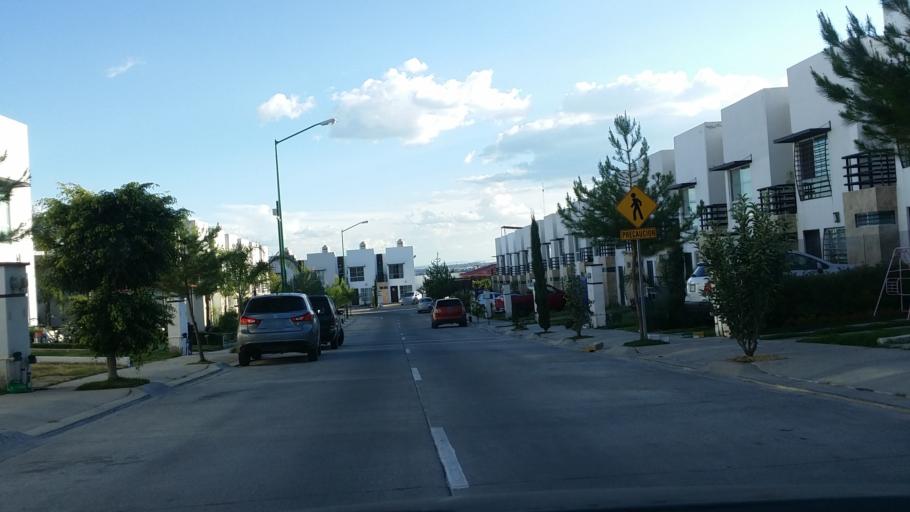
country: MX
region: Guanajuato
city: Leon
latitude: 21.2006
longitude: -101.6789
